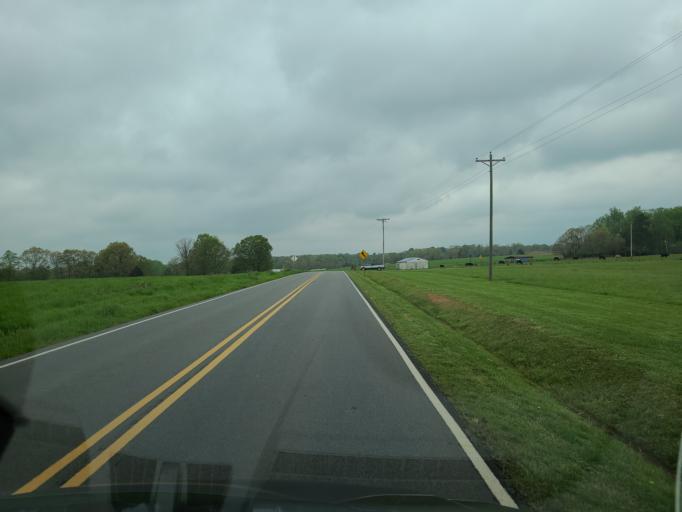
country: US
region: North Carolina
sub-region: Gaston County
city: Cherryville
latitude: 35.4553
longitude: -81.3428
